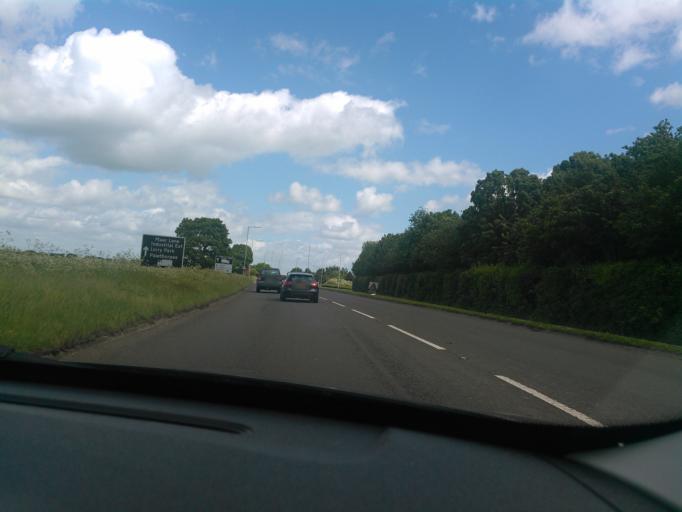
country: GB
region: England
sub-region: Shropshire
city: Market Drayton
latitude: 52.8952
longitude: -2.5233
